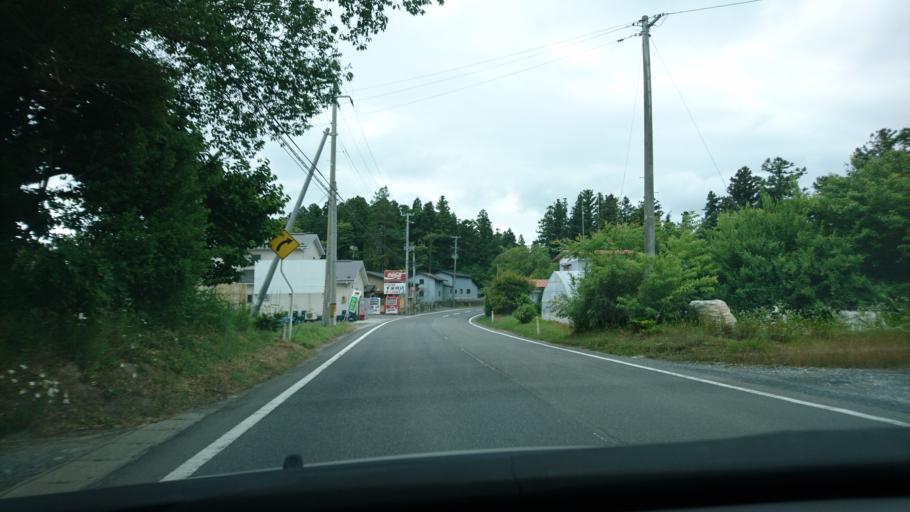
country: JP
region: Iwate
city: Ichinoseki
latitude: 38.7530
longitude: 141.2548
